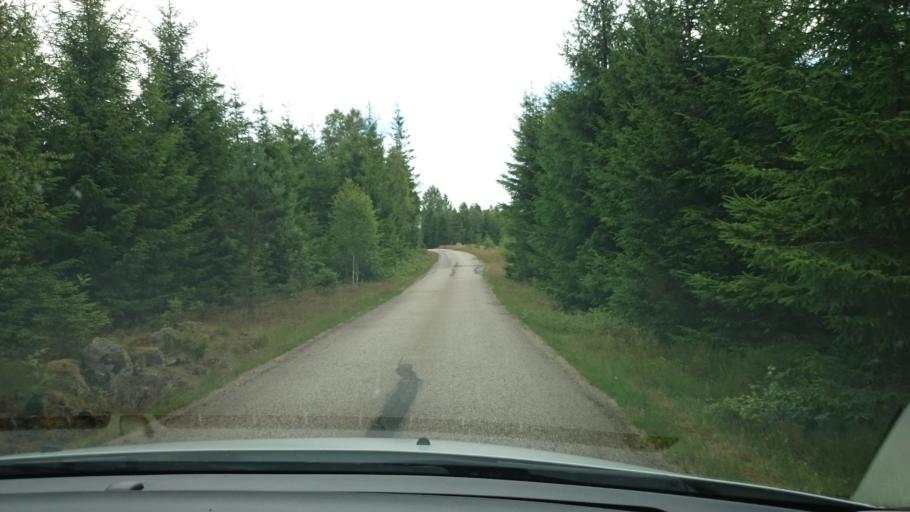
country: SE
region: Halland
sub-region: Hylte Kommun
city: Hyltebruk
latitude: 56.9738
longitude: 13.2030
